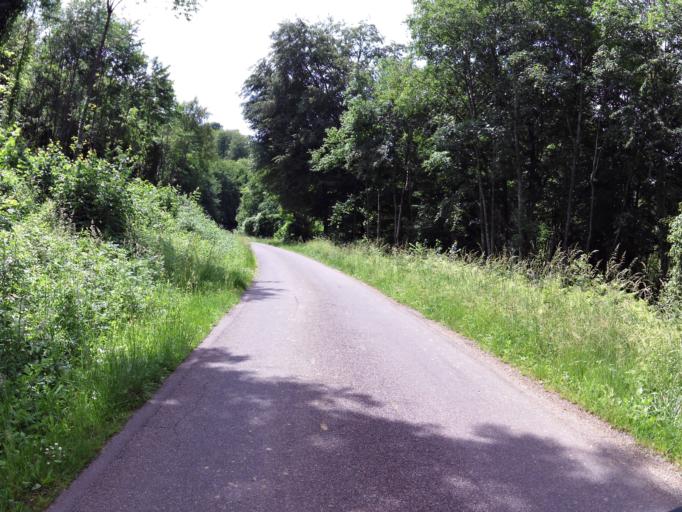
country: FR
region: Lorraine
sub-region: Departement de la Meuse
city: Stenay
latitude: 49.5396
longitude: 5.1390
